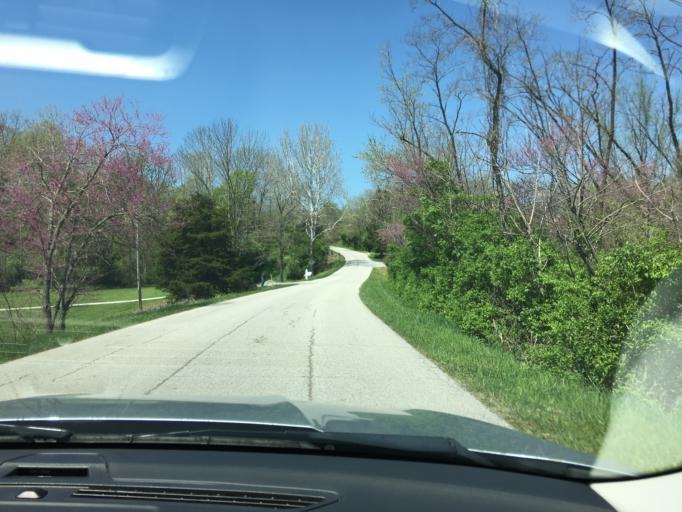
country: US
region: Indiana
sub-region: Tippecanoe County
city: Dayton
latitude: 40.3139
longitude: -86.7503
